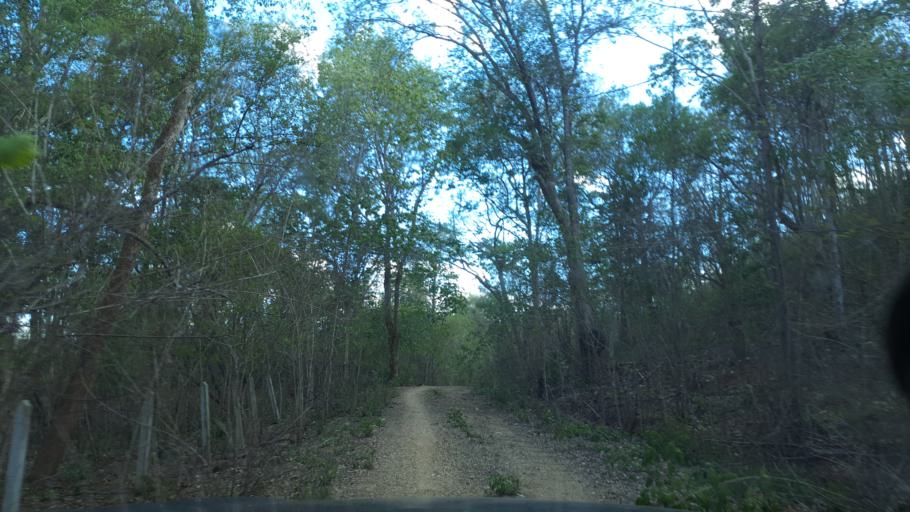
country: TH
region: Lampang
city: Sop Prap
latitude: 17.8391
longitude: 99.2851
